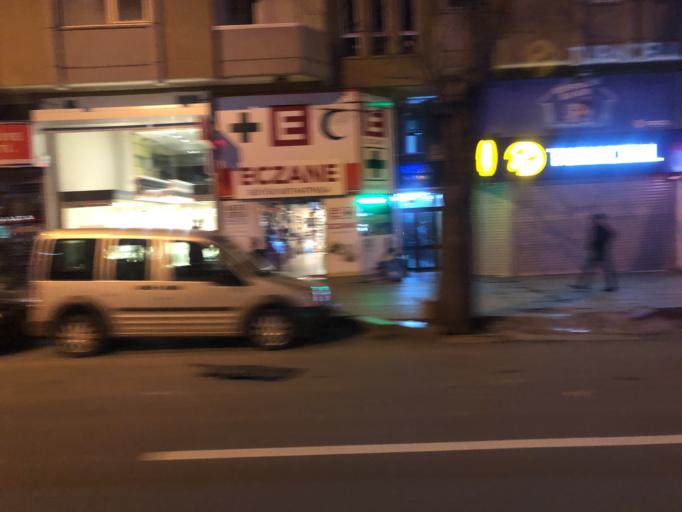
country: TR
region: Ankara
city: Ankara
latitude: 39.9231
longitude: 32.8573
